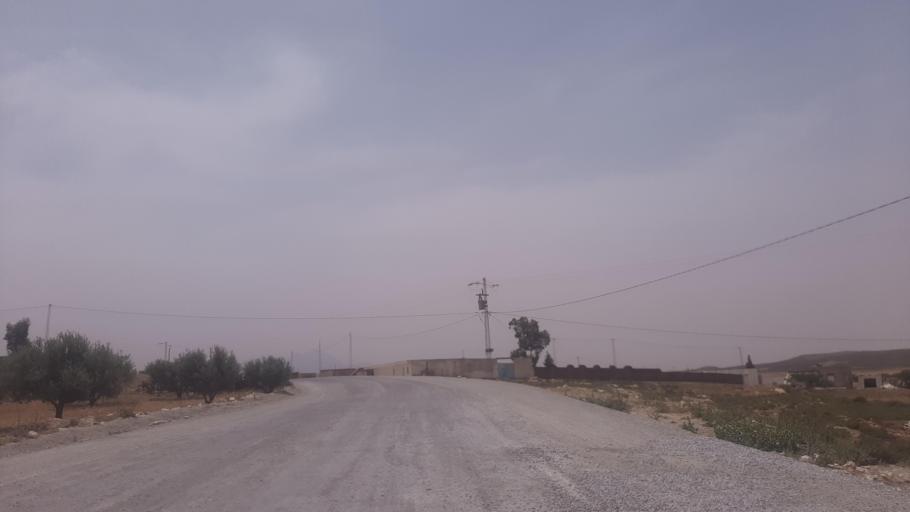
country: TN
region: Zaghwan
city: Zaghouan
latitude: 36.5261
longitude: 10.1590
